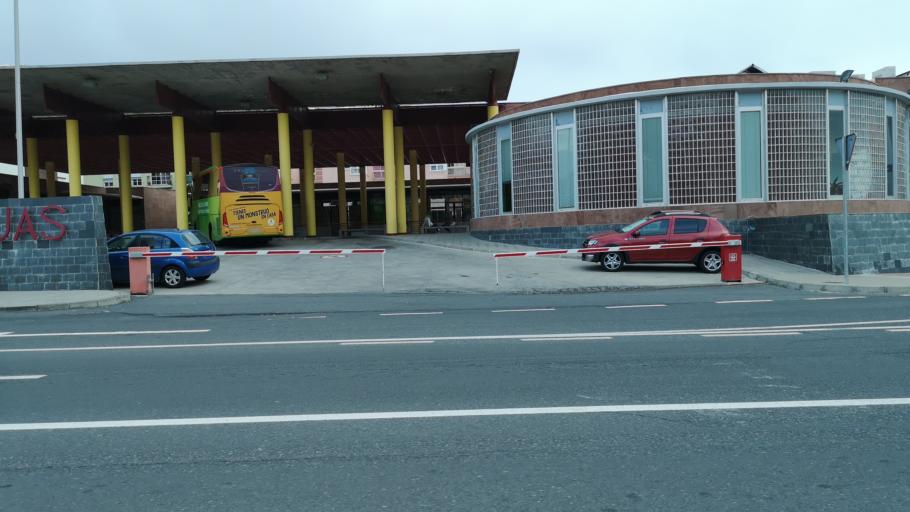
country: ES
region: Canary Islands
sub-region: Provincia de Santa Cruz de Tenerife
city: San Sebastian de la Gomera
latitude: 28.0916
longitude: -17.1139
